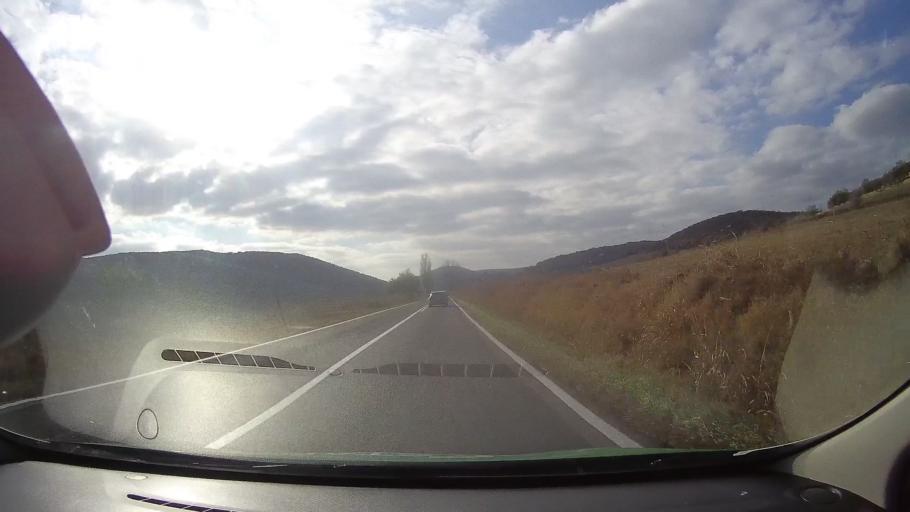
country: RO
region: Tulcea
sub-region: Comuna Nalbant
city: Nicolae Balcescu
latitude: 44.9692
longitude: 28.5375
